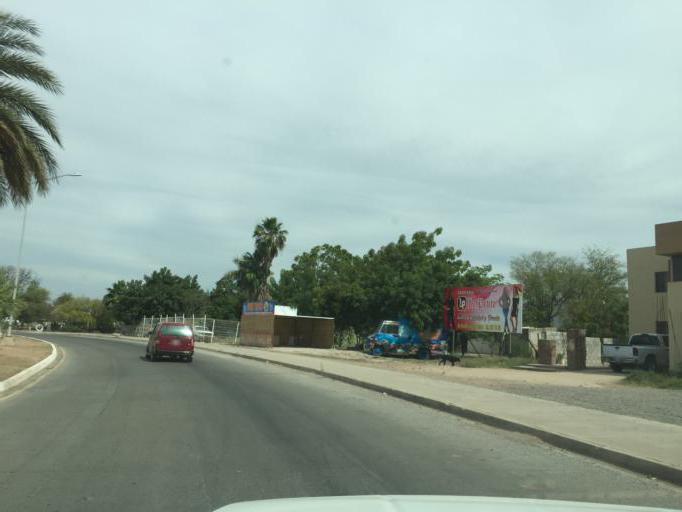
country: MX
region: Sonora
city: Navojoa
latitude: 27.0836
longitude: -109.4574
